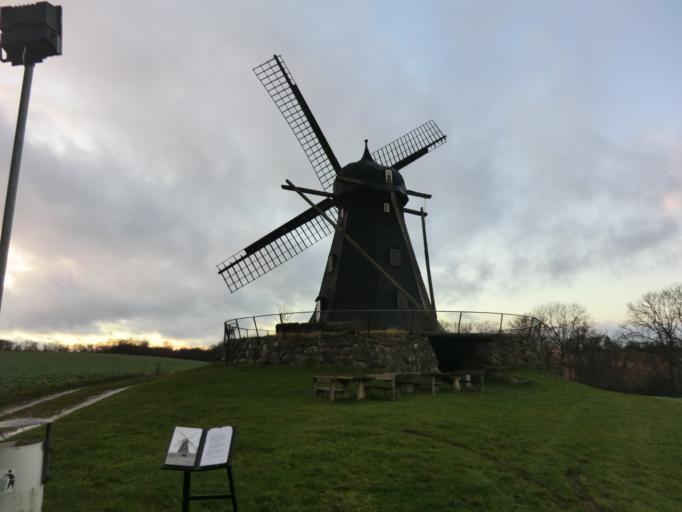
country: SE
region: Skane
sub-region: Lunds Kommun
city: Genarp
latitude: 55.7154
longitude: 13.3368
